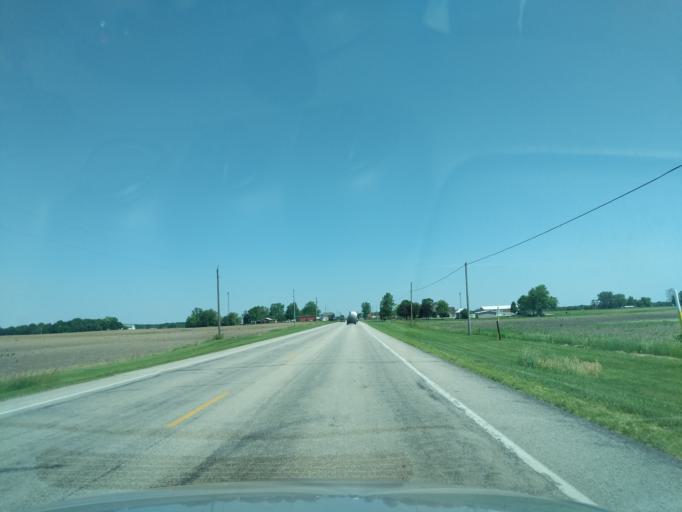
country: US
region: Indiana
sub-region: Whitley County
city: Columbia City
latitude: 41.0714
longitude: -85.4703
